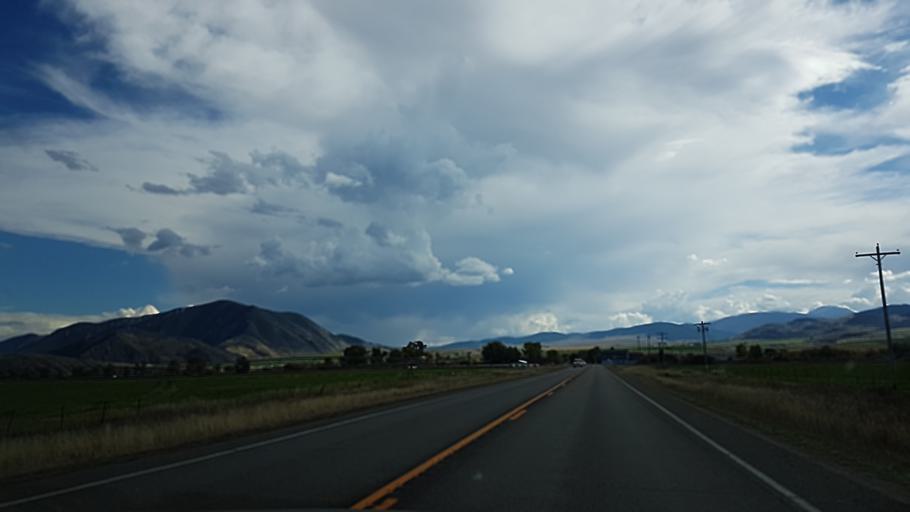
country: US
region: Montana
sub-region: Jefferson County
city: Whitehall
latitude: 45.8645
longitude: -111.9536
